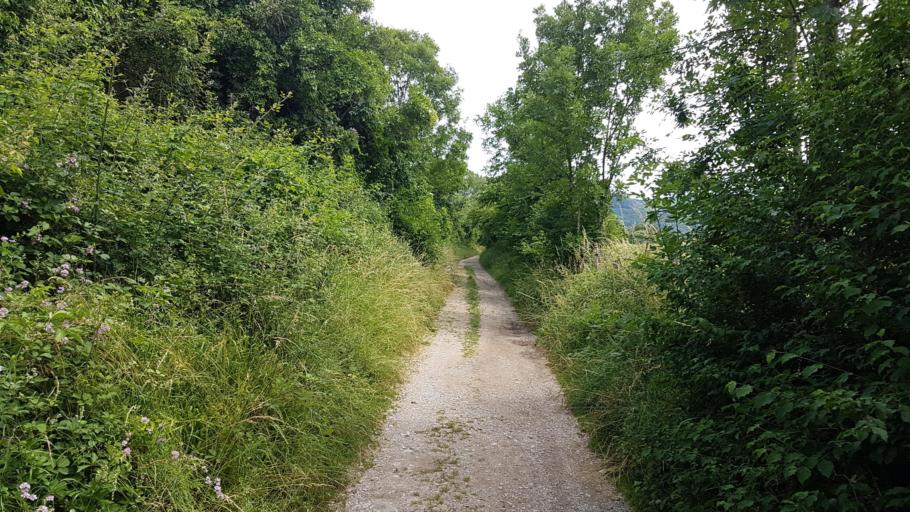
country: FR
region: Franche-Comte
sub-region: Departement du Jura
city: Perrigny
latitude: 46.6671
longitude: 5.5794
